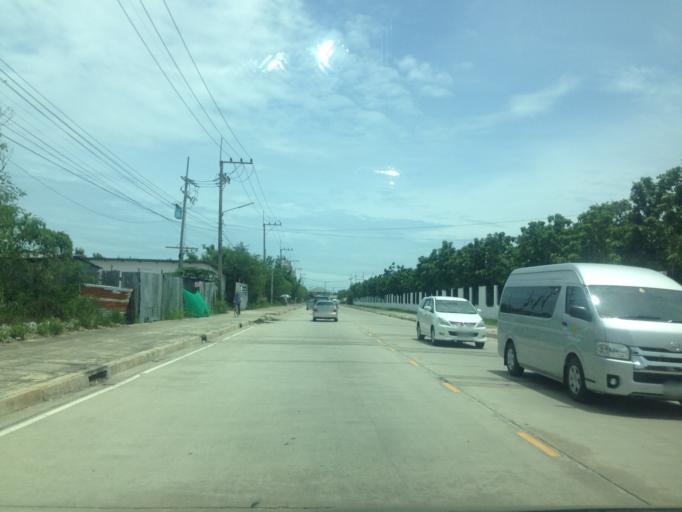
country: TH
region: Chon Buri
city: Chon Buri
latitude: 13.3467
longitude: 100.9624
